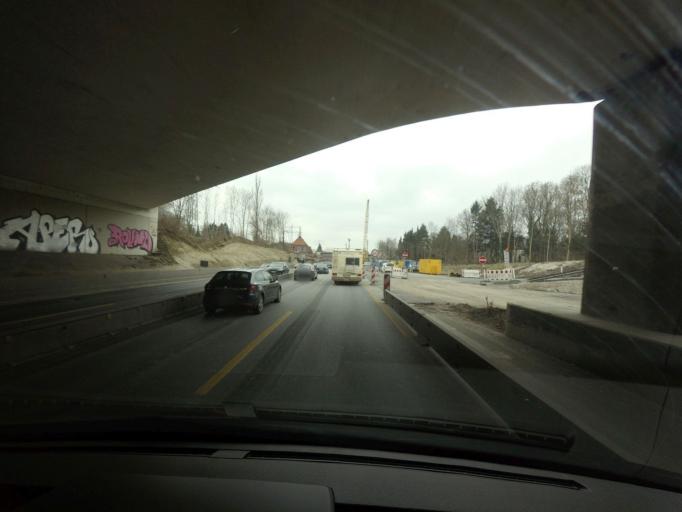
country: DE
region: Hamburg
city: Eidelstedt
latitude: 53.6340
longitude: 9.9236
